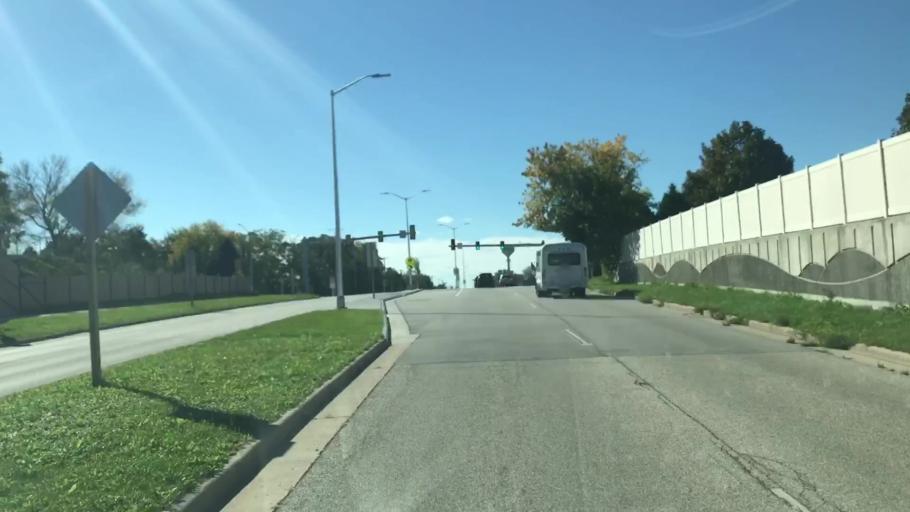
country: US
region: Wisconsin
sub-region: Waukesha County
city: Pewaukee
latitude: 43.0455
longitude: -88.2859
